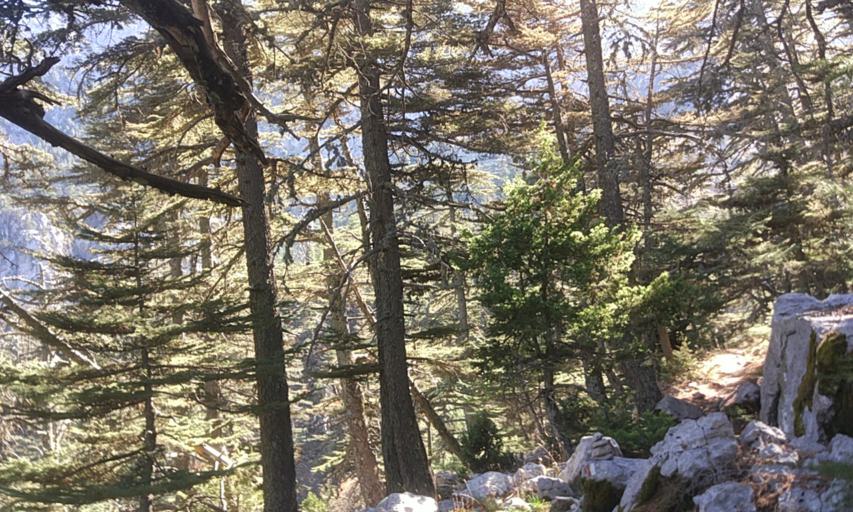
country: TR
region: Antalya
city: Altinyaka
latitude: 36.5560
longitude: 30.4161
